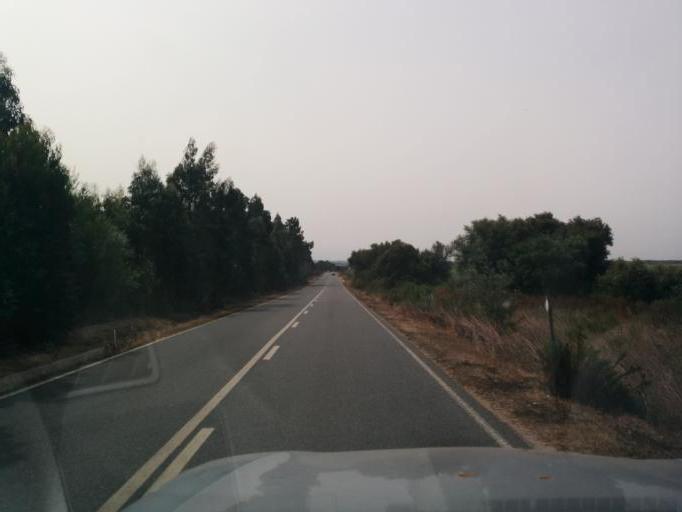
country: PT
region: Beja
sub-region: Odemira
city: Sao Teotonio
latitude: 37.6011
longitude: -8.7444
